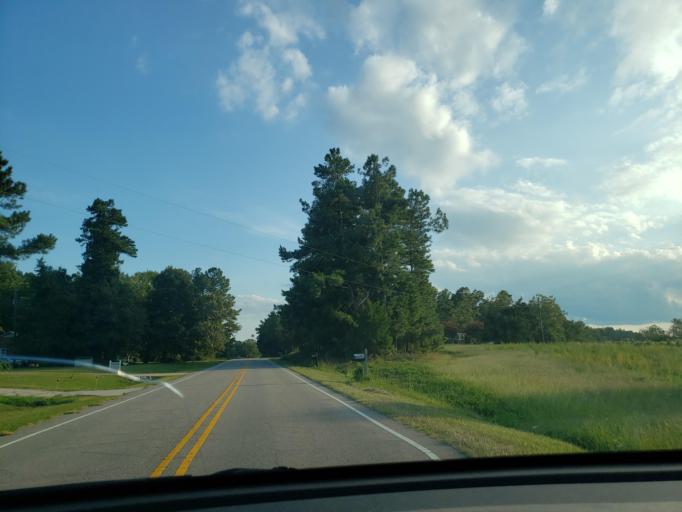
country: US
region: North Carolina
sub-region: Vance County
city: Henderson
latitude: 36.3692
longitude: -78.3727
